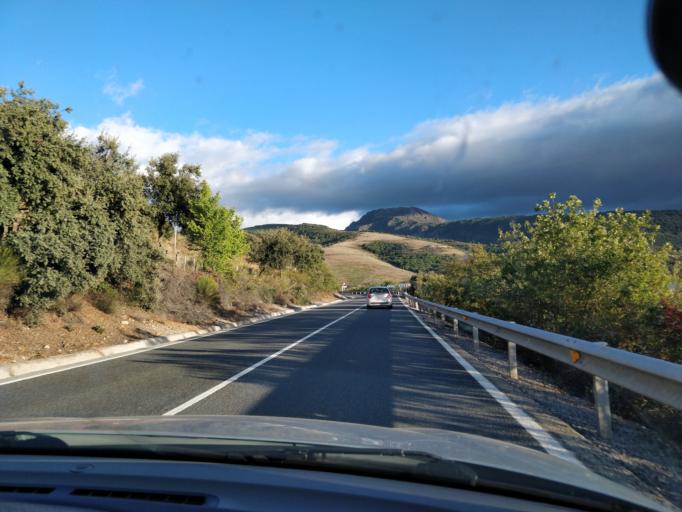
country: ES
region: Castille and Leon
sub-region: Provincia de Leon
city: Borrenes
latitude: 42.4950
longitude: -6.7171
